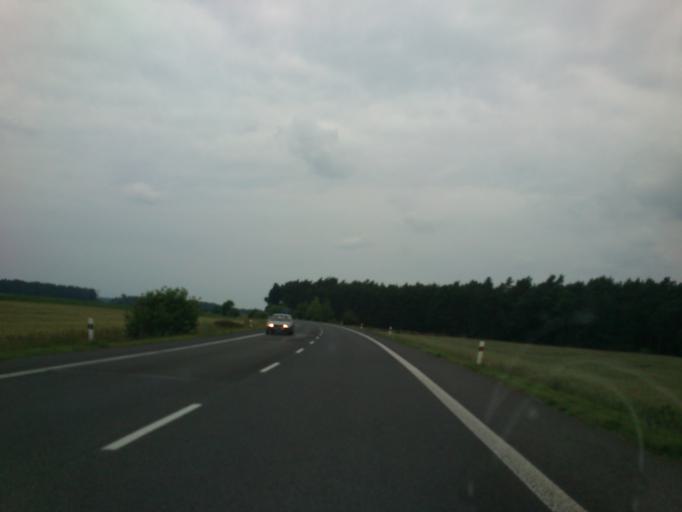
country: CZ
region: Central Bohemia
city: Bela pod Bezdezem
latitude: 50.4812
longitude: 14.8524
